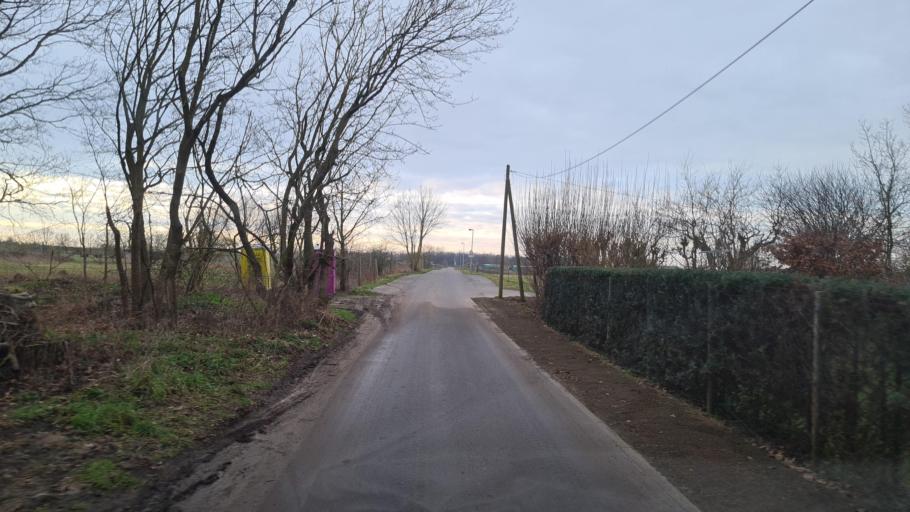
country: DE
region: Brandenburg
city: Stahnsdorf
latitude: 52.3655
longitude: 13.2123
